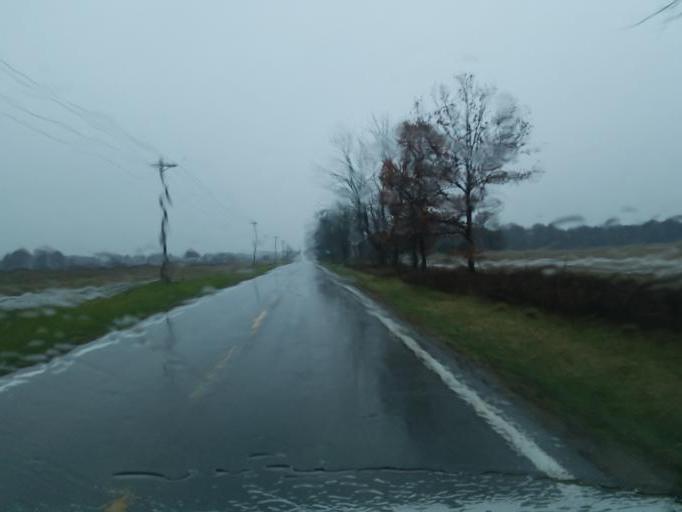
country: US
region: Ohio
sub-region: Delaware County
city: Sunbury
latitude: 40.3260
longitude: -82.9016
